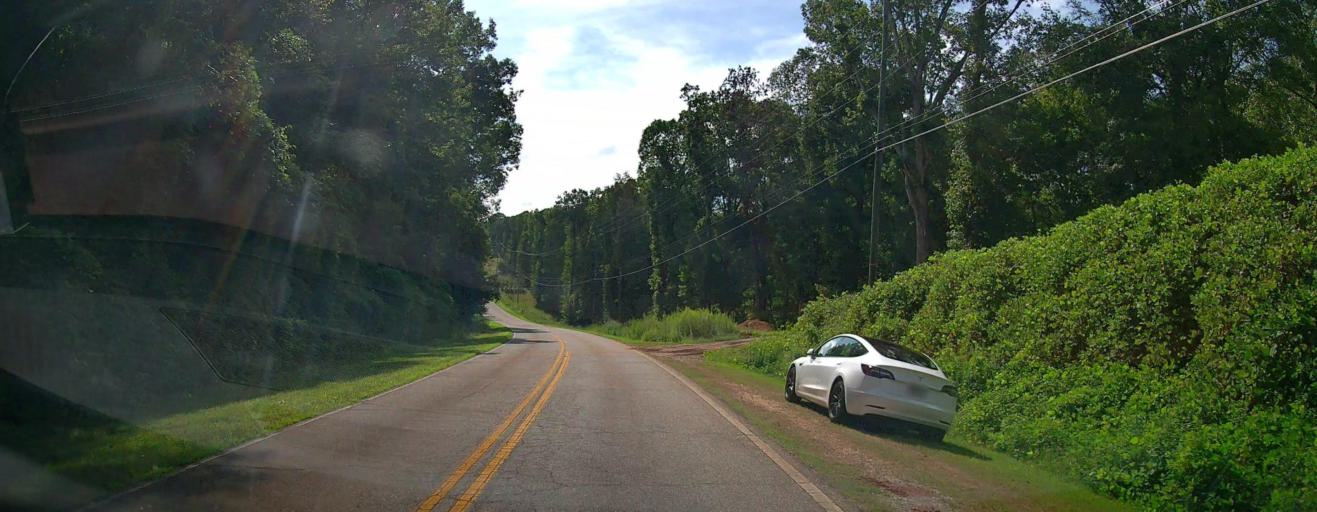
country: US
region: Alabama
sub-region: Russell County
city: Phenix City
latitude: 32.6074
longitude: -84.9652
